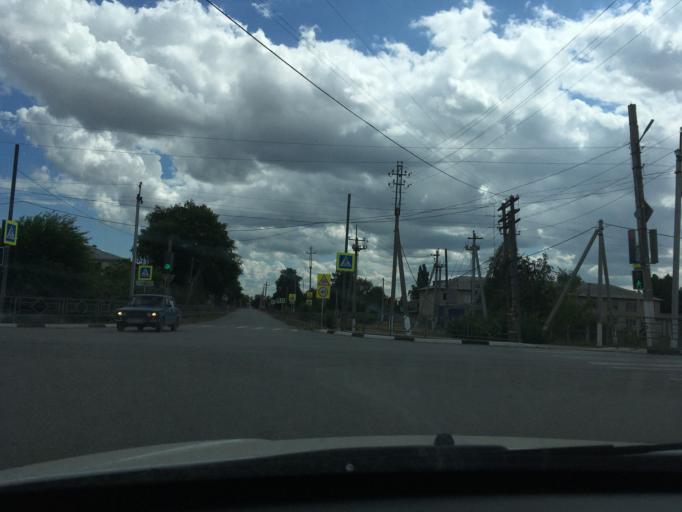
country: RU
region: Samara
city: Bezenchuk
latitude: 52.9872
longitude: 49.4344
